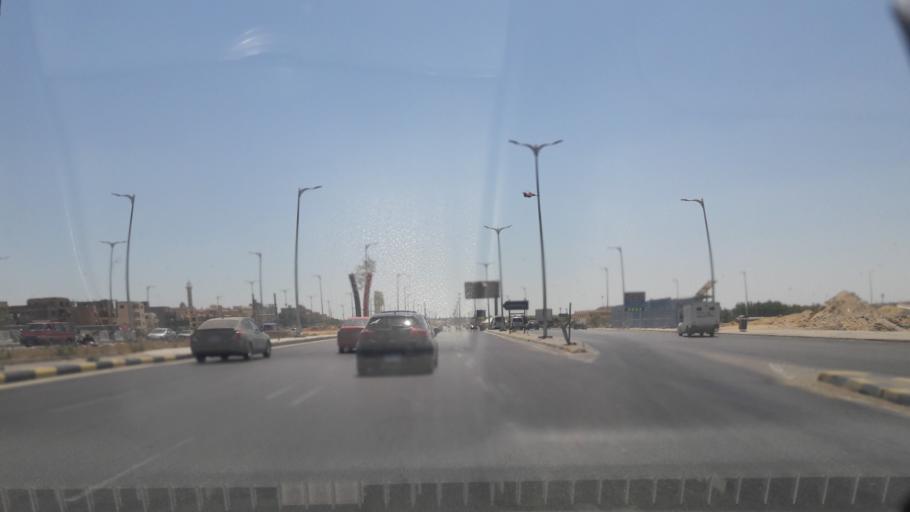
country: EG
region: Al Jizah
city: Madinat Sittah Uktubar
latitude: 29.9954
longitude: 30.9612
